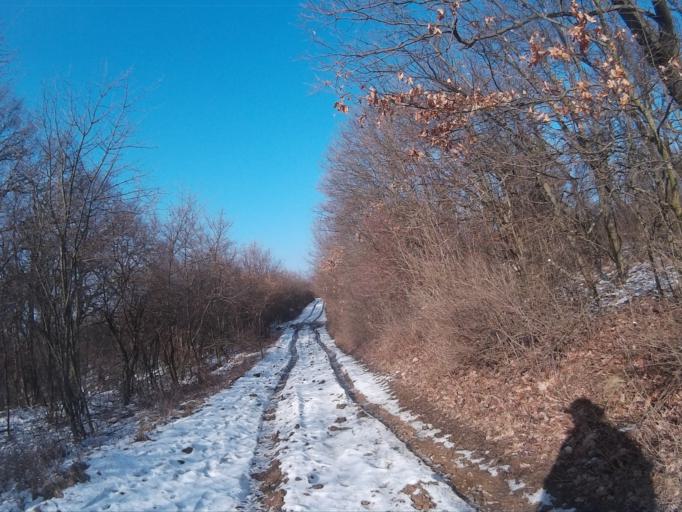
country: HU
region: Komarom-Esztergom
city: Labatlan
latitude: 47.7141
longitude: 18.4943
